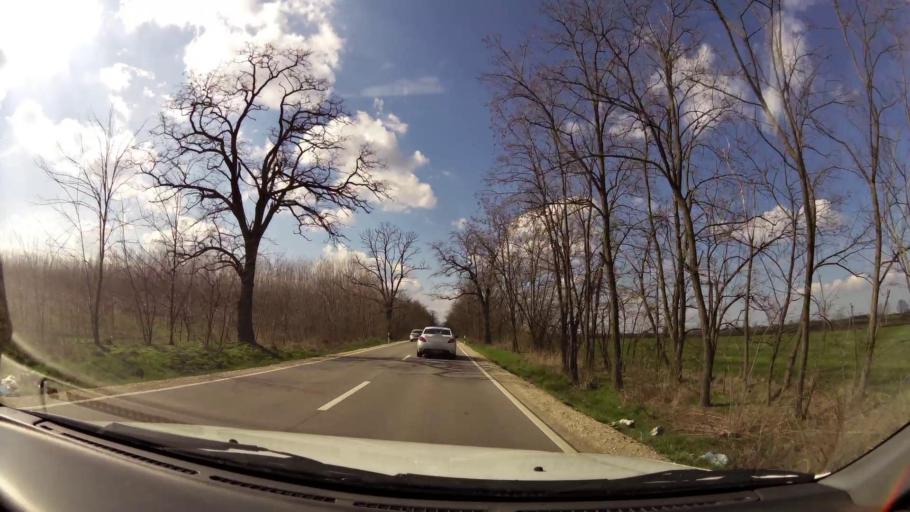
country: HU
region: Pest
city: Forropuszta
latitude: 47.4607
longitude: 19.6582
